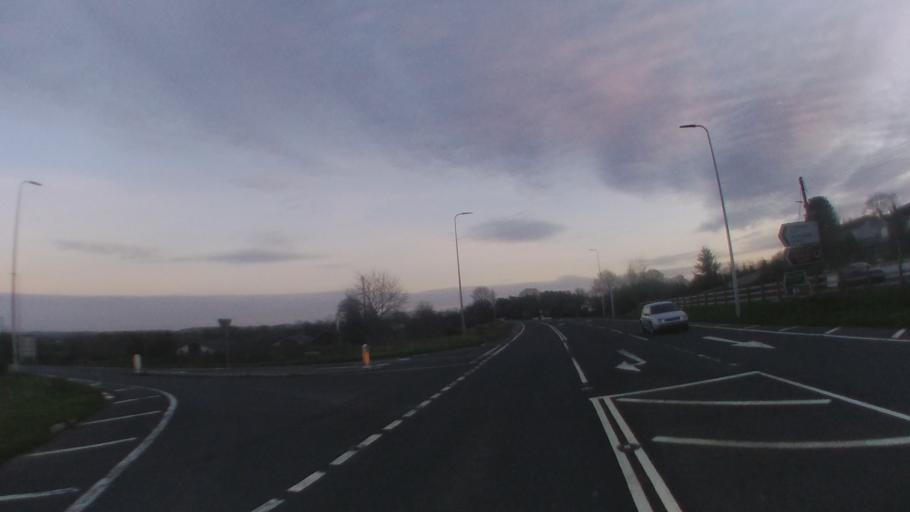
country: GB
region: Northern Ireland
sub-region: Armagh District
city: Tandragee
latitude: 54.2960
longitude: -6.5147
